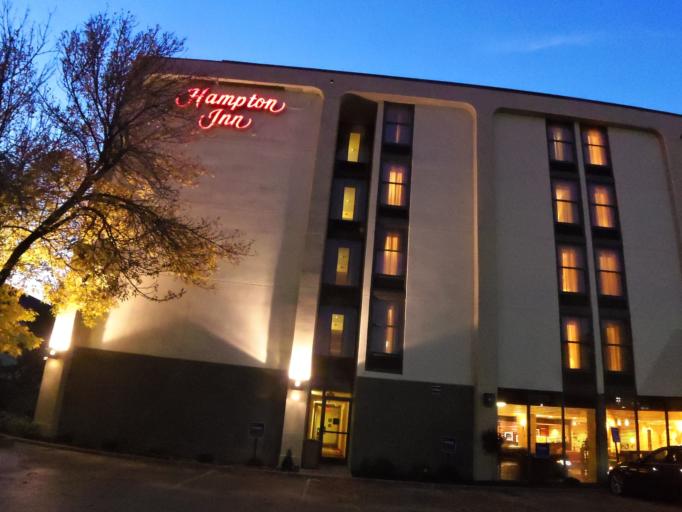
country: US
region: Kentucky
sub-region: Fayette County
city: Lexington-Fayette
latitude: 38.0434
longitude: -84.4236
